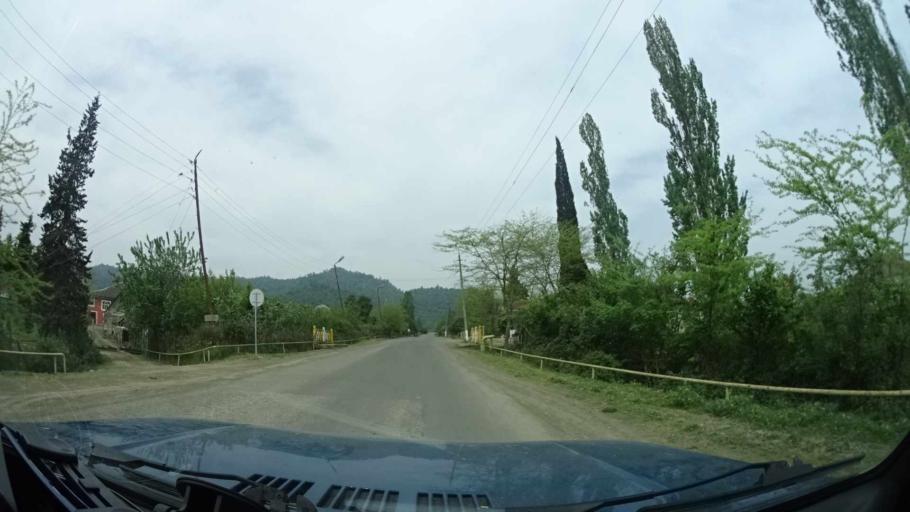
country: AZ
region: Lankaran
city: Haftoni
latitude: 38.7461
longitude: 48.7842
